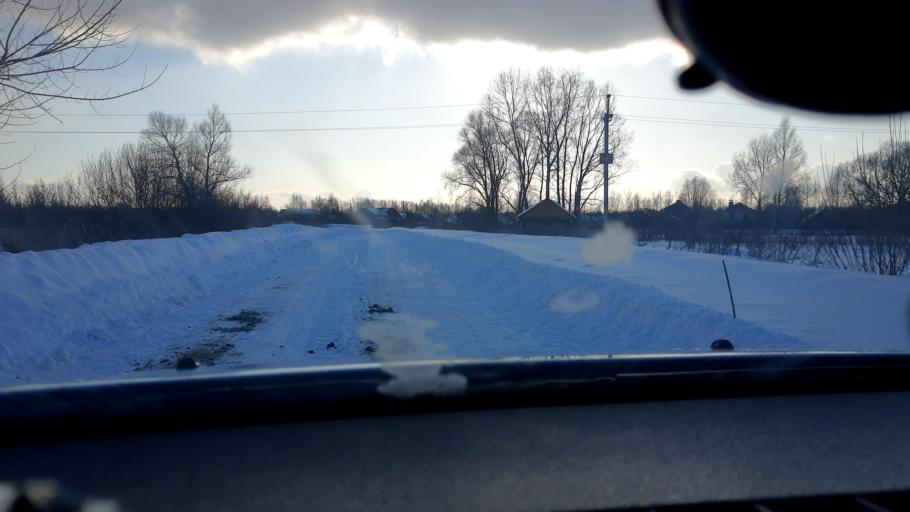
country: RU
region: Bashkortostan
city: Ufa
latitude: 54.6534
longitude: 56.0650
